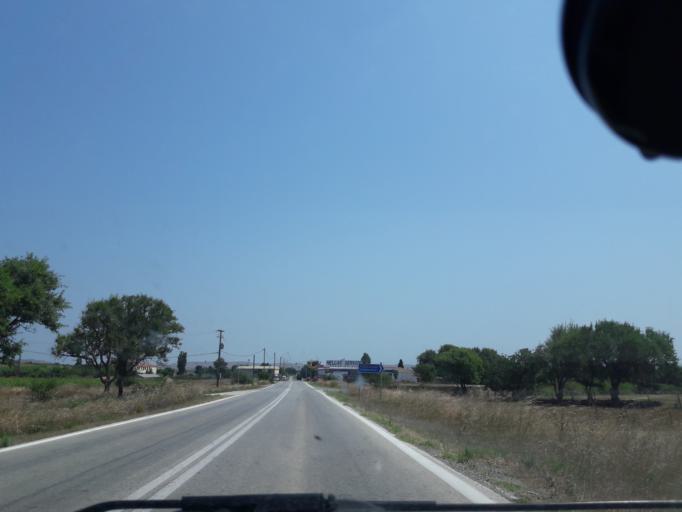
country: GR
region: North Aegean
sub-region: Nomos Lesvou
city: Myrina
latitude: 39.9117
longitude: 25.1960
